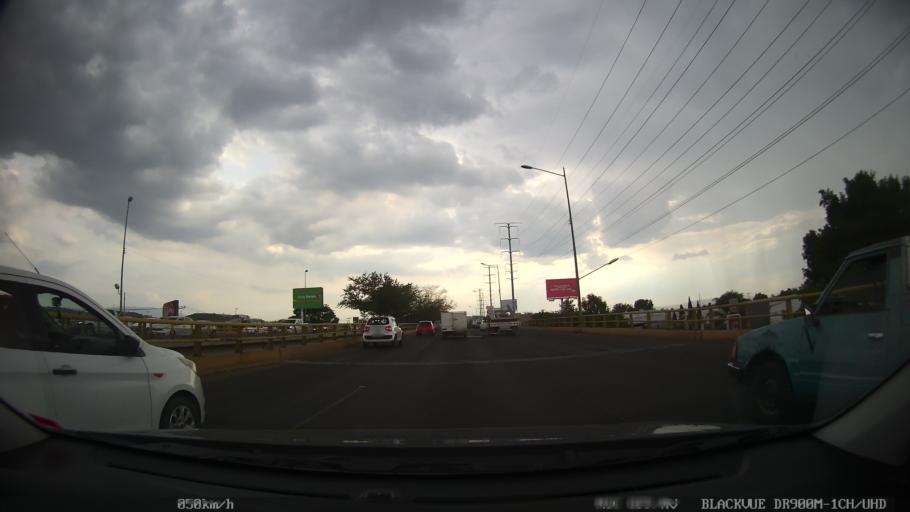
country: MX
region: Jalisco
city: Tlaquepaque
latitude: 20.6262
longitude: -103.3034
